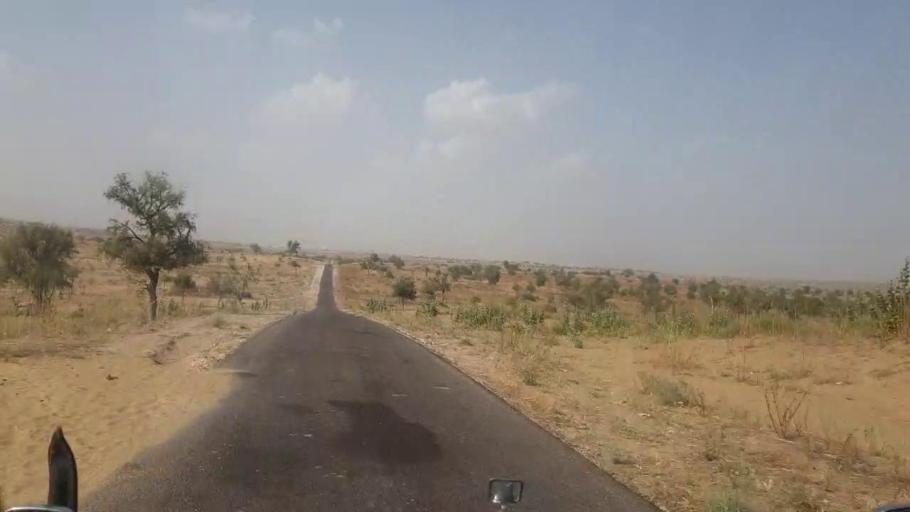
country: PK
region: Sindh
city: Islamkot
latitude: 25.1940
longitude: 70.2849
